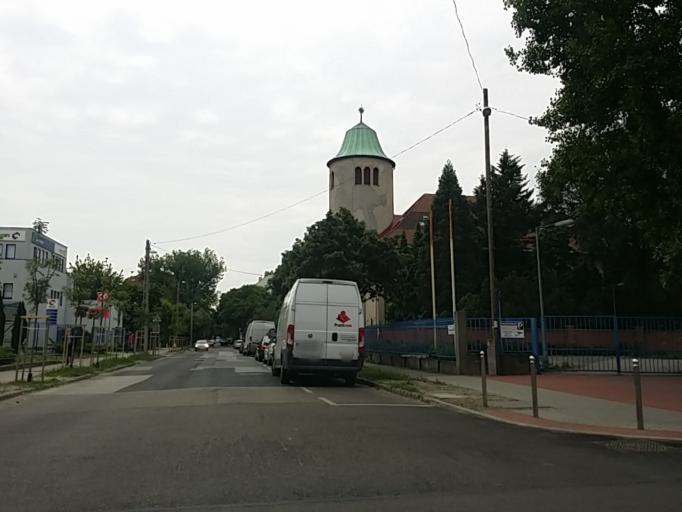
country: HU
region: Budapest
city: Budapest XIII. keruelet
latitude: 47.5348
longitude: 19.0776
